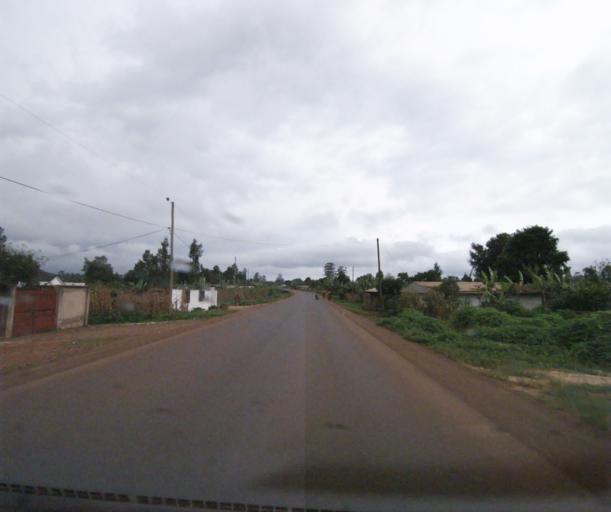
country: CM
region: West
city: Dschang
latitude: 5.4926
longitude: 10.1641
